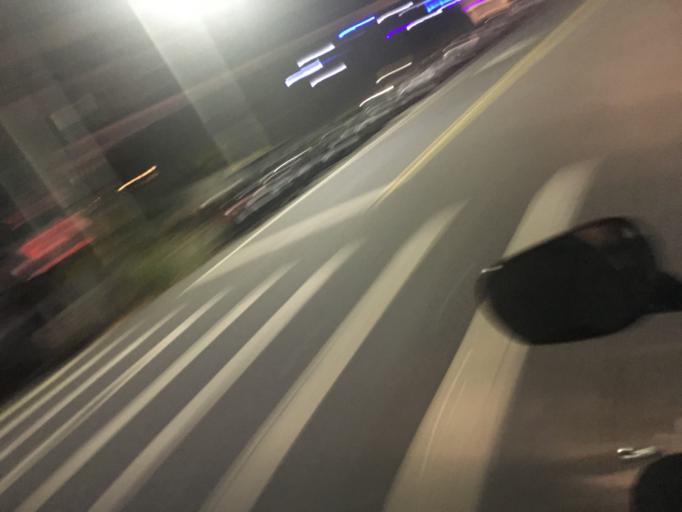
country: TW
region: Taiwan
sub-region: Hsinchu
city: Hsinchu
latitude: 24.7769
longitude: 120.9674
